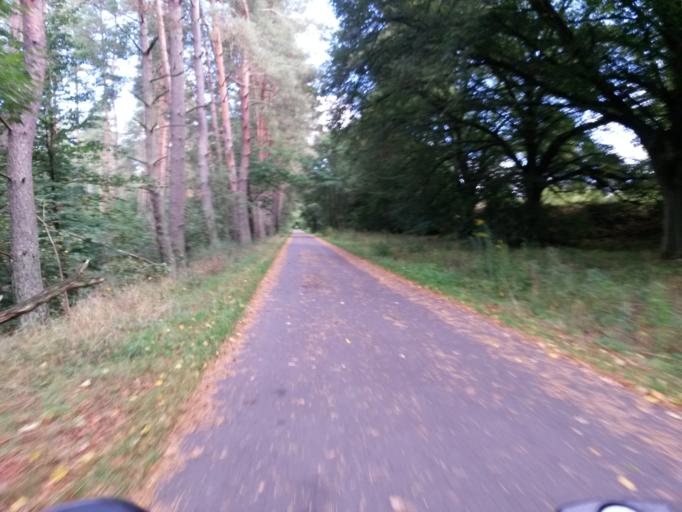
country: DE
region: Brandenburg
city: Templin
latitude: 53.1837
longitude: 13.5134
